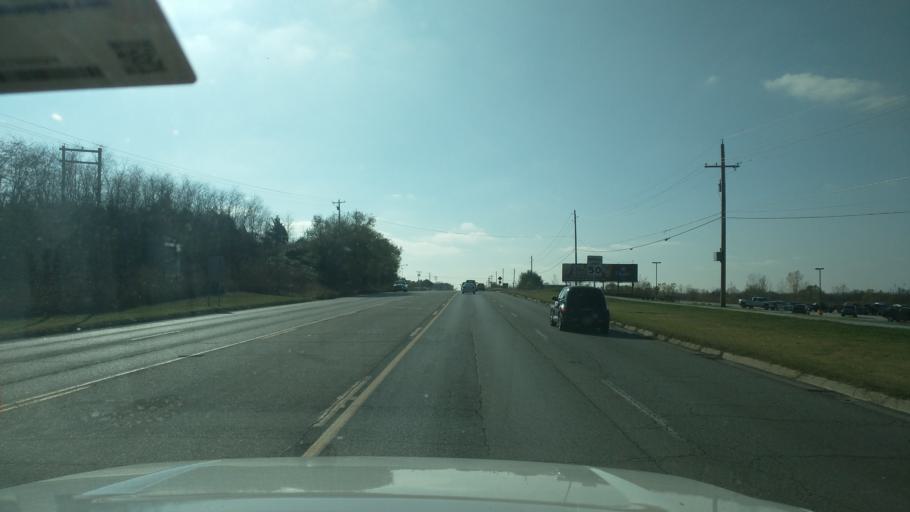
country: US
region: Oklahoma
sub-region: Washington County
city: Bartlesville
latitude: 36.7042
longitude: -95.9352
